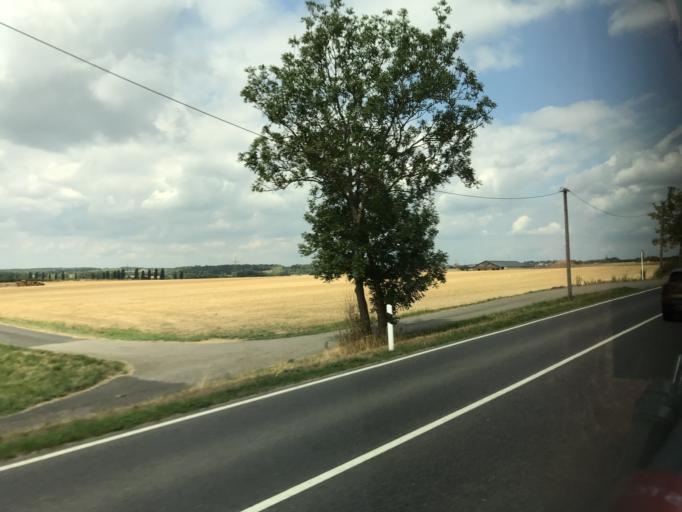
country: LU
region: Luxembourg
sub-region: Canton de Luxembourg
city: Alzingen
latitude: 49.5541
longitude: 6.1709
